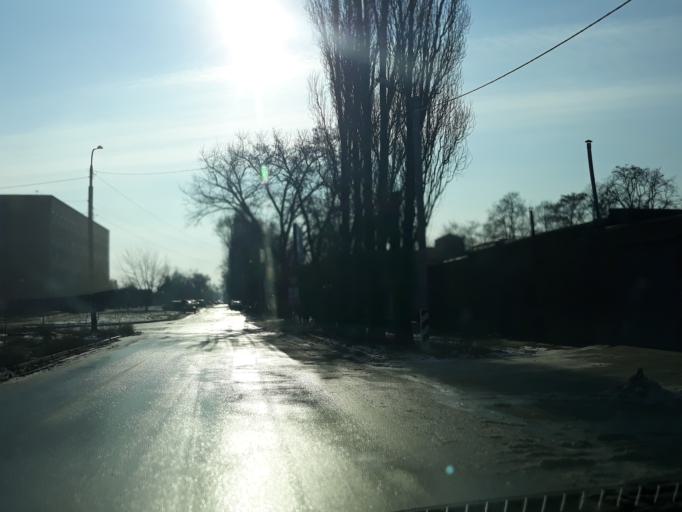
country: RU
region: Rostov
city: Taganrog
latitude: 47.2265
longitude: 38.9077
